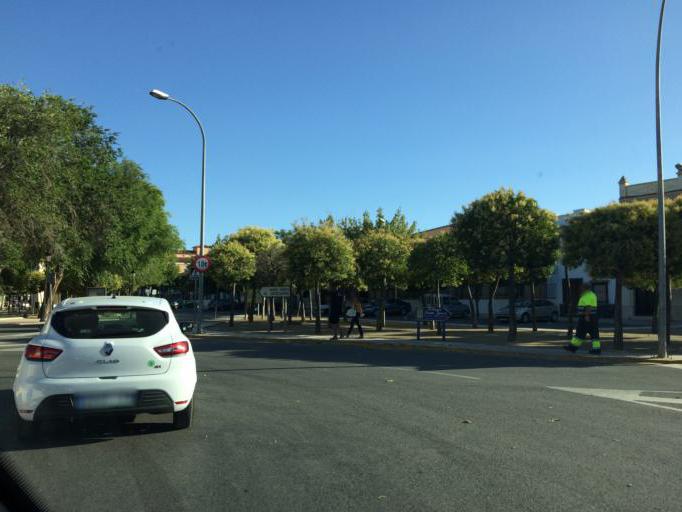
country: ES
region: Andalusia
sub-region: Provincia de Malaga
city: Campillos
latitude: 37.0447
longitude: -4.8607
